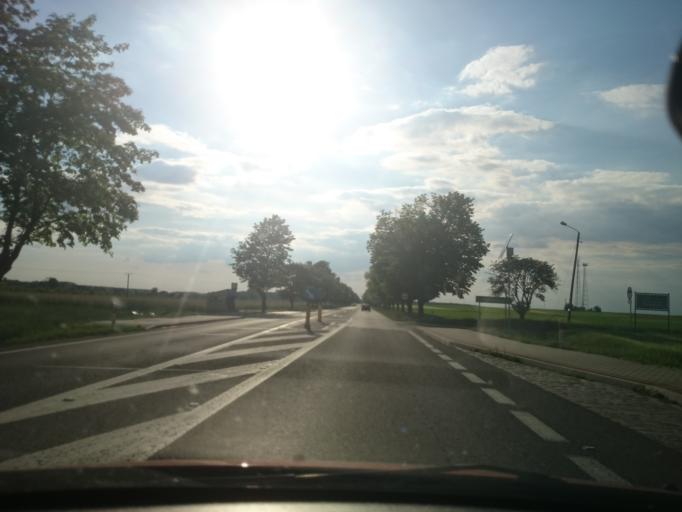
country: PL
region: Opole Voivodeship
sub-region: Powiat strzelecki
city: Izbicko
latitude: 50.5585
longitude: 18.2008
